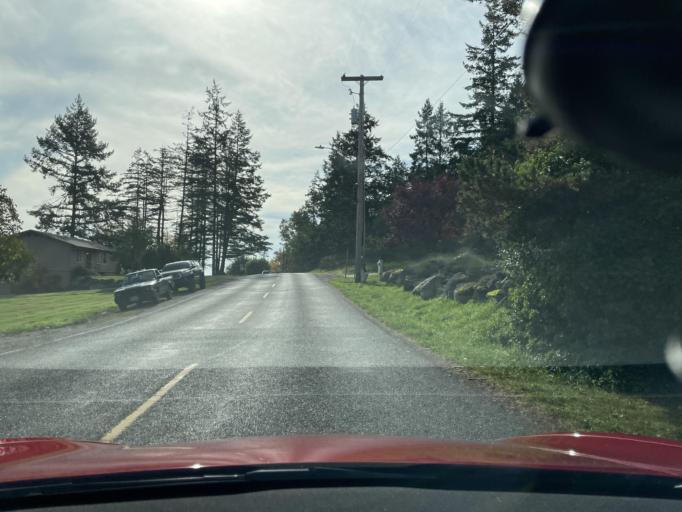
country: US
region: Washington
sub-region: San Juan County
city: Friday Harbor
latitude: 48.5335
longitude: -123.0269
